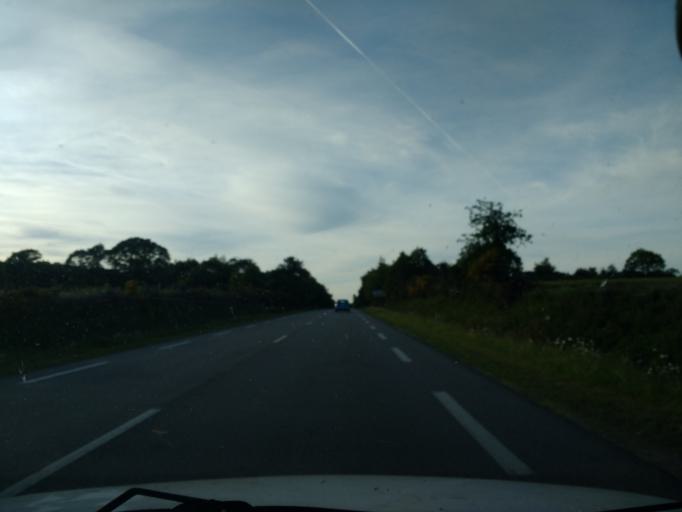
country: FR
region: Brittany
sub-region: Departement du Morbihan
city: Questembert
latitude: 47.6424
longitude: -2.4258
